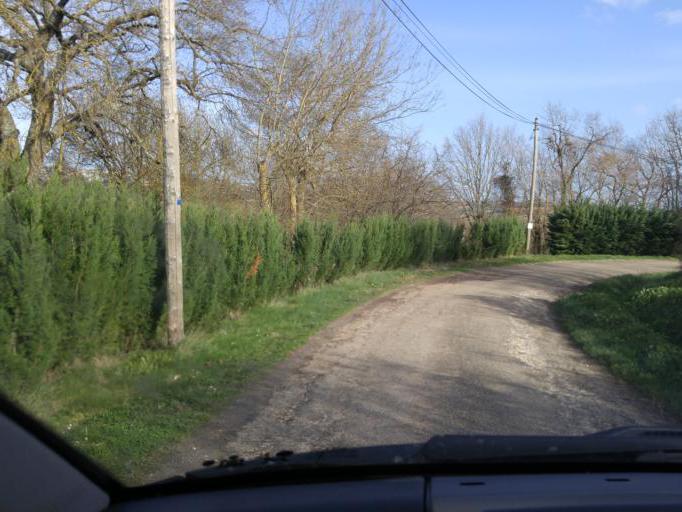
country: FR
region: Midi-Pyrenees
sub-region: Departement du Gers
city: Lectoure
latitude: 43.9247
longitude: 0.6003
